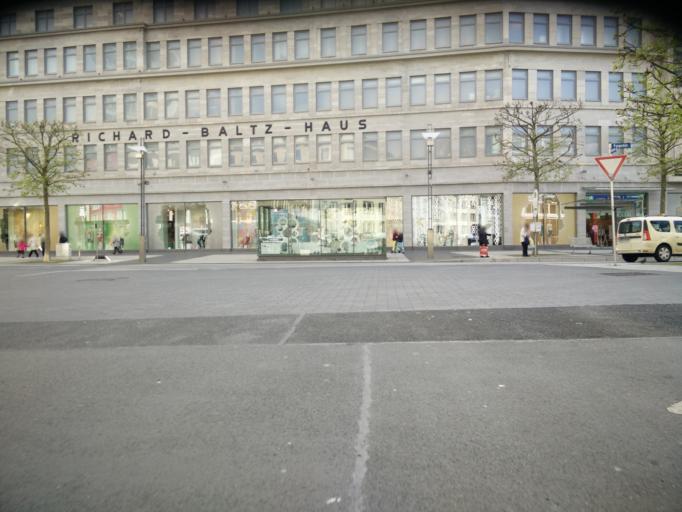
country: DE
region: North Rhine-Westphalia
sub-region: Regierungsbezirk Arnsberg
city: Bochum
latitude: 51.4813
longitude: 7.2204
